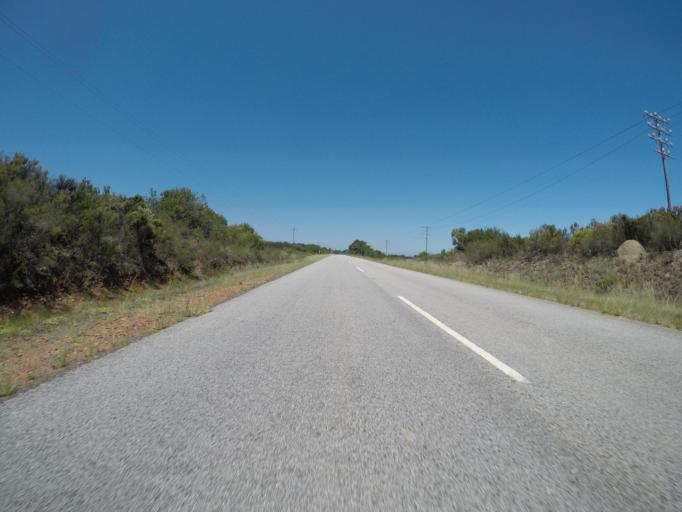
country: ZA
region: Eastern Cape
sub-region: Cacadu District Municipality
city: Kareedouw
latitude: -33.9599
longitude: 24.4165
